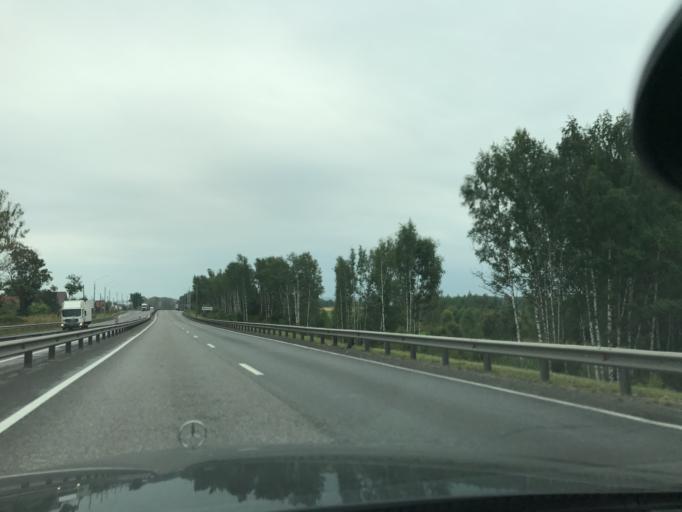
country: RU
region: Vladimir
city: Novovyazniki
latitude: 56.1849
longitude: 42.3995
